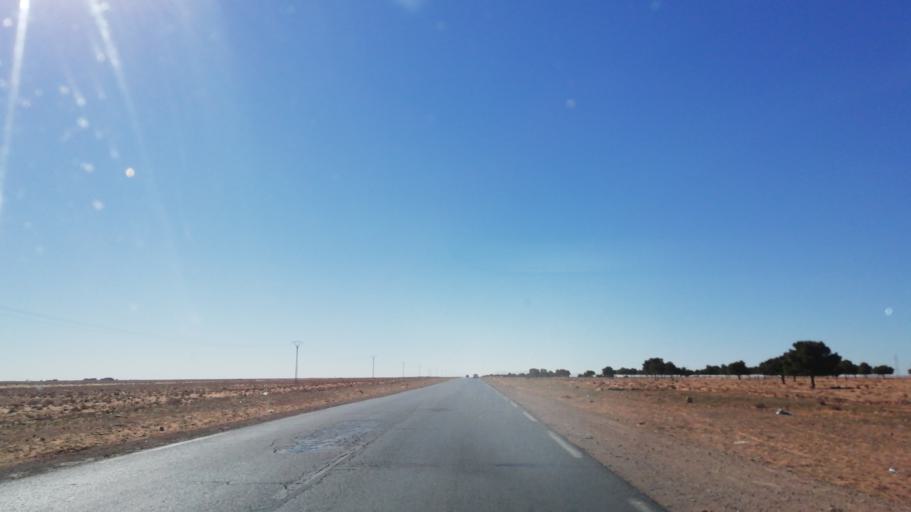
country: DZ
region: Saida
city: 'Ain el Hadjar
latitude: 33.9938
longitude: 0.0380
